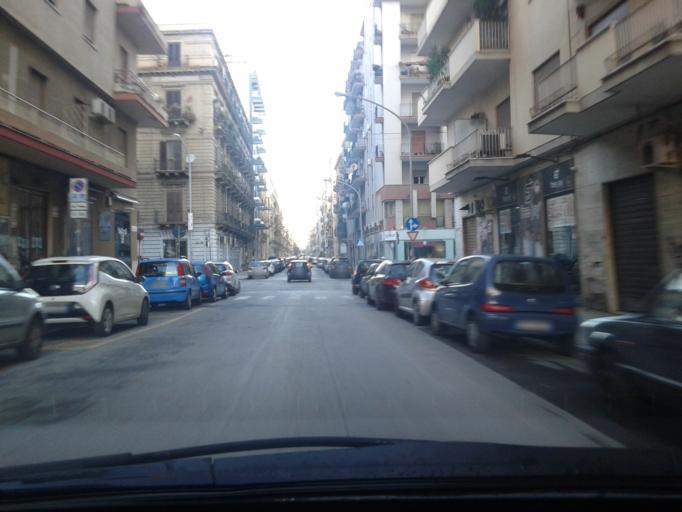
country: IT
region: Sicily
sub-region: Palermo
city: Palermo
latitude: 38.1179
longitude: 13.3462
